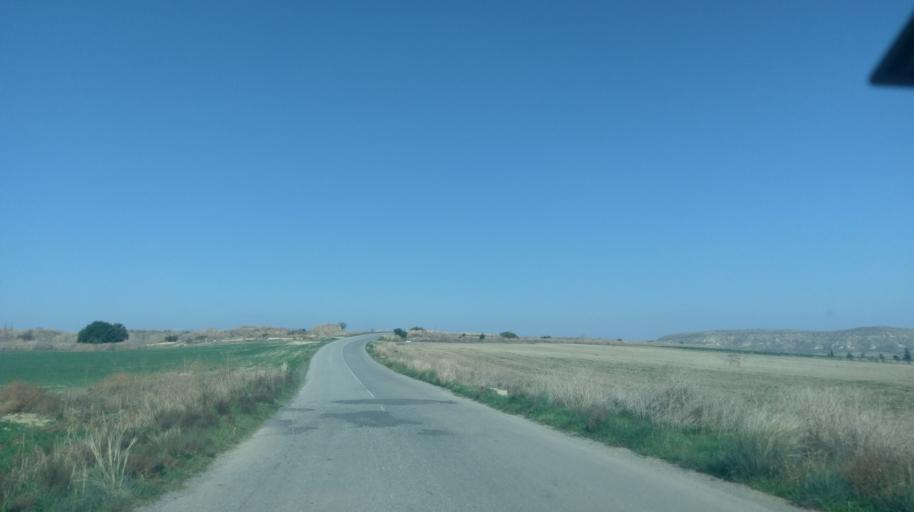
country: CY
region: Larnaka
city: Athienou
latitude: 35.0682
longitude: 33.4835
